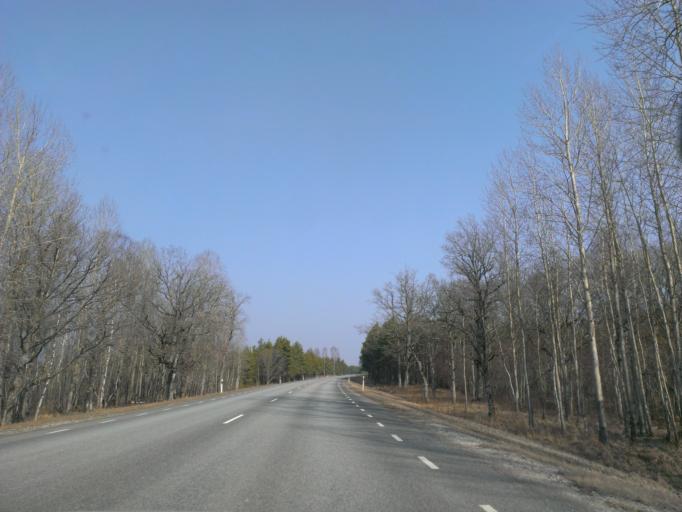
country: EE
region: Saare
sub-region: Orissaare vald
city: Orissaare
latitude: 58.4899
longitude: 22.8455
